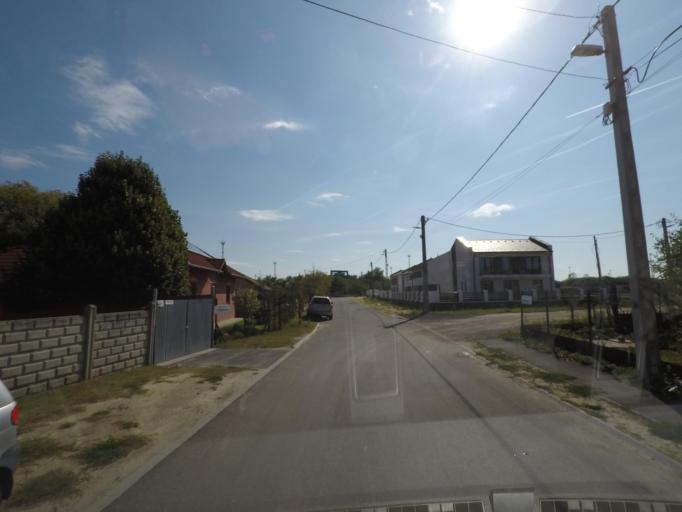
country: HU
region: Budapest
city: Budapest XXIII. keruelet
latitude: 47.3821
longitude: 19.1171
